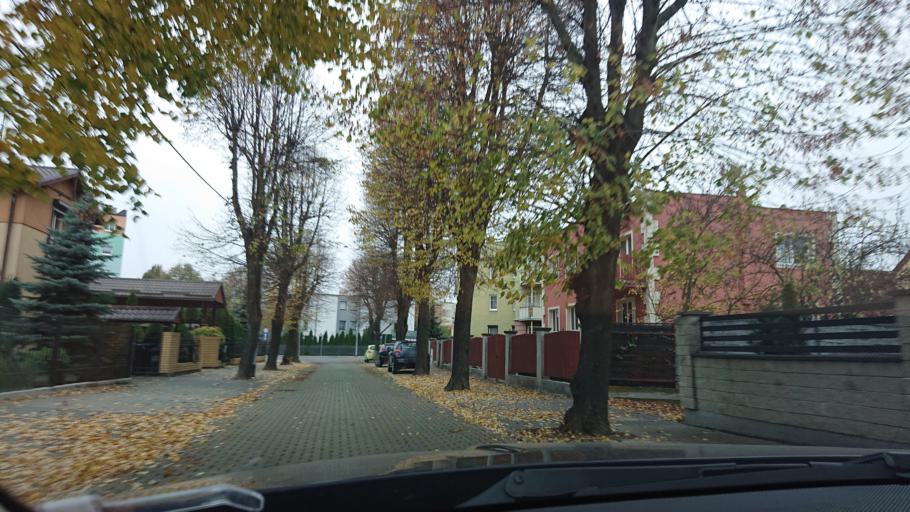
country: PL
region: Greater Poland Voivodeship
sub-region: Powiat gnieznienski
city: Gniezno
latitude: 52.5338
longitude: 17.6203
